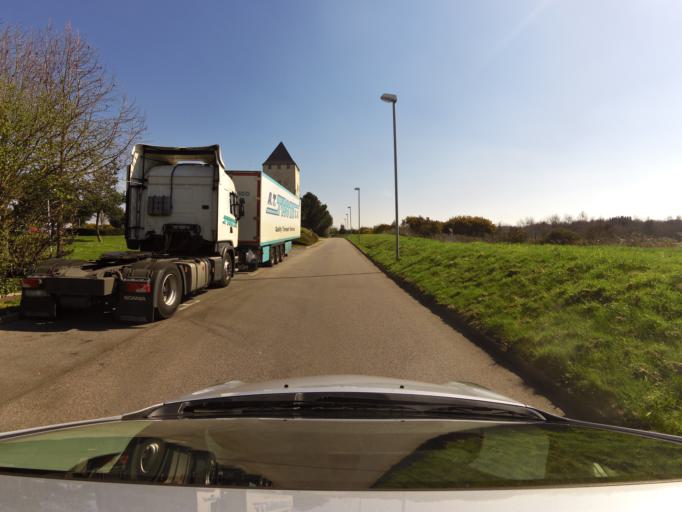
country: FR
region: Brittany
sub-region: Departement du Morbihan
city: Ploermel
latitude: 47.9193
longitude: -2.3655
